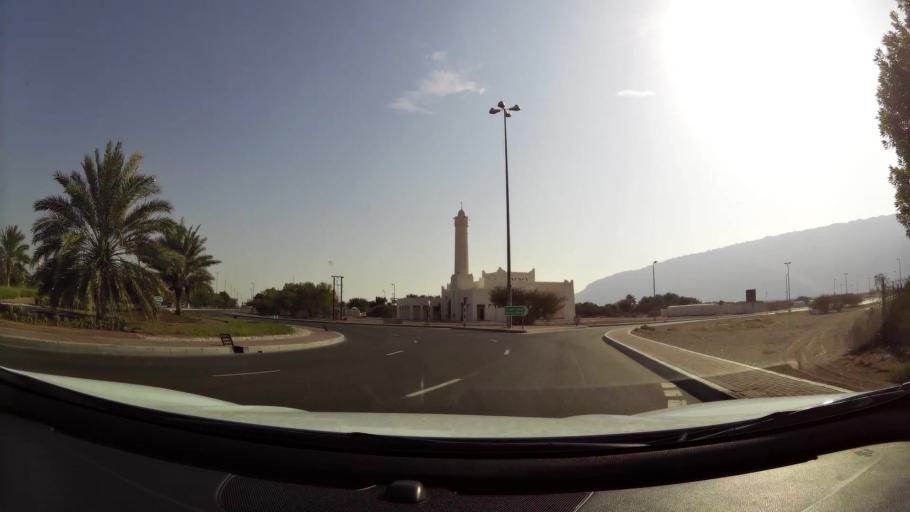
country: AE
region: Abu Dhabi
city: Al Ain
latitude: 24.0451
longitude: 55.8421
